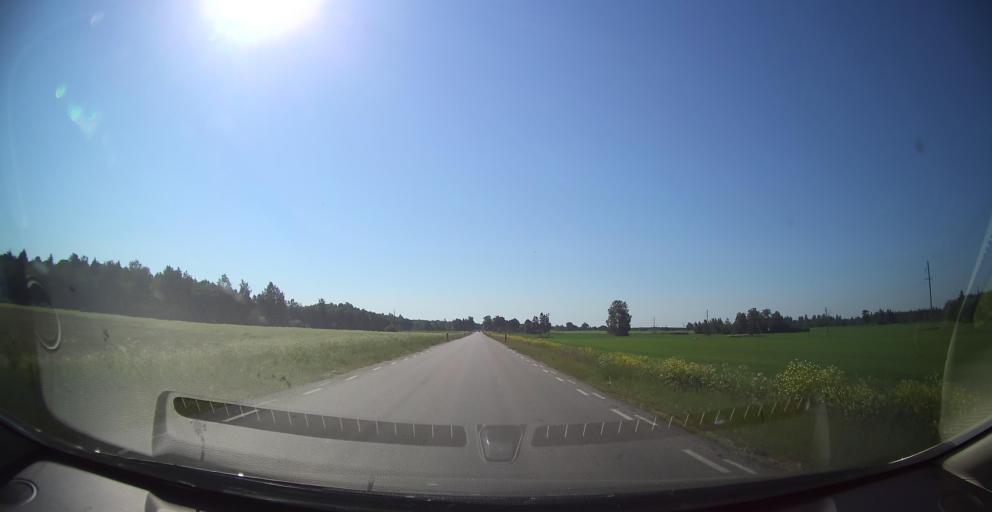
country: EE
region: Harju
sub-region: Raasiku vald
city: Raasiku
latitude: 59.3113
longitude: 25.1566
